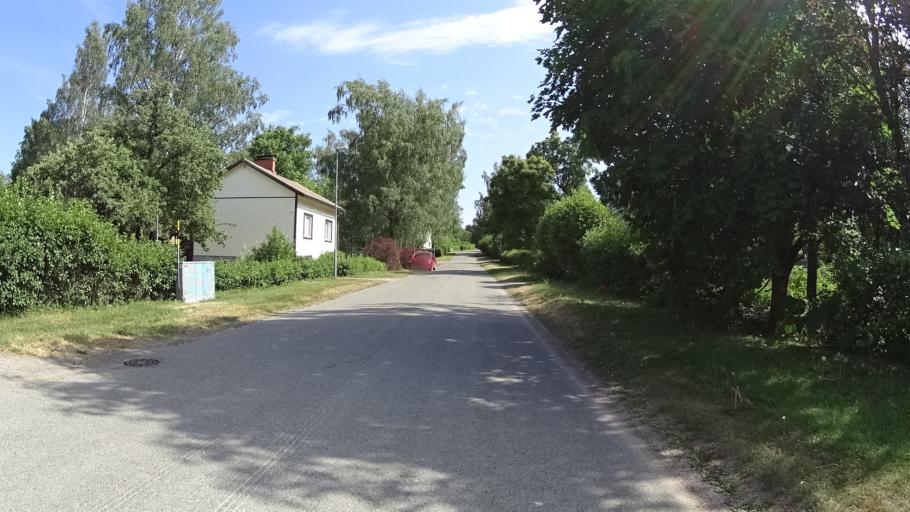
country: FI
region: Uusimaa
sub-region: Raaseporin
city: Karis
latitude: 60.0747
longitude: 23.6673
